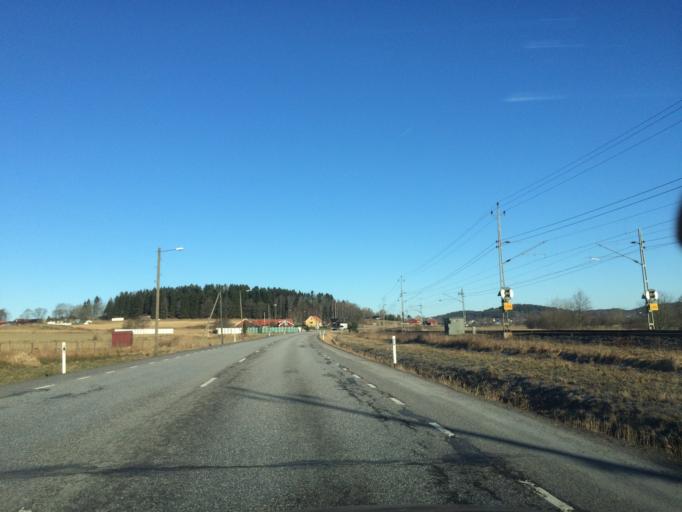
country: SE
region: Vaestra Goetaland
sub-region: Molndal
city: Lindome
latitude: 57.5582
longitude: 12.0854
